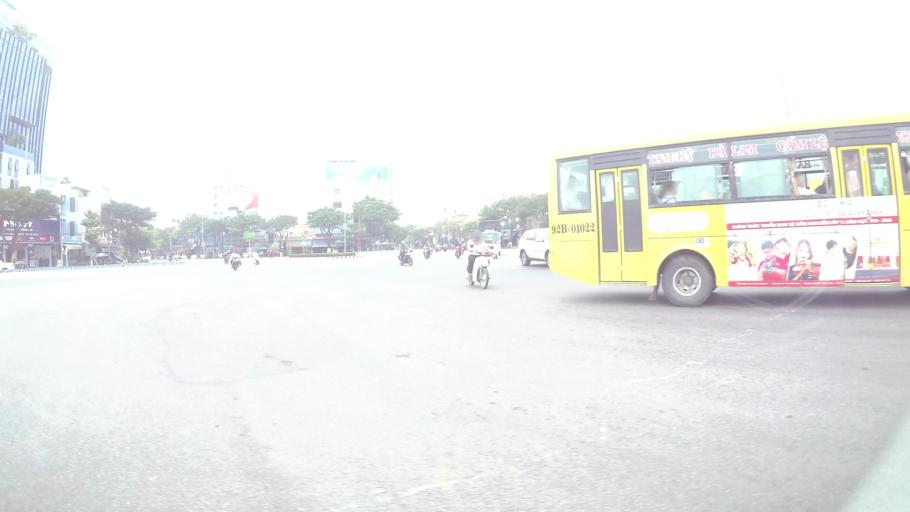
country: VN
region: Da Nang
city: Da Nang
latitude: 16.0505
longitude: 108.2089
